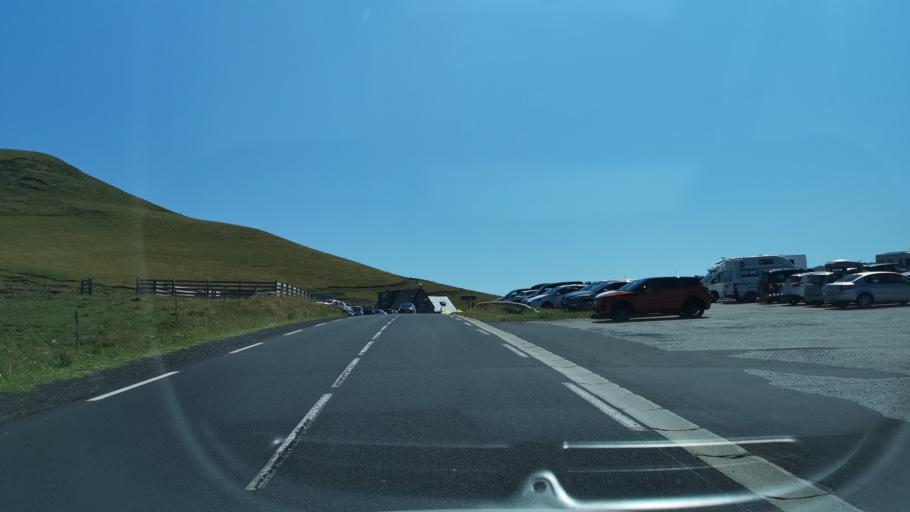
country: FR
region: Auvergne
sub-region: Departement du Puy-de-Dome
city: Mont-Dore
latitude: 45.5974
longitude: 2.8503
